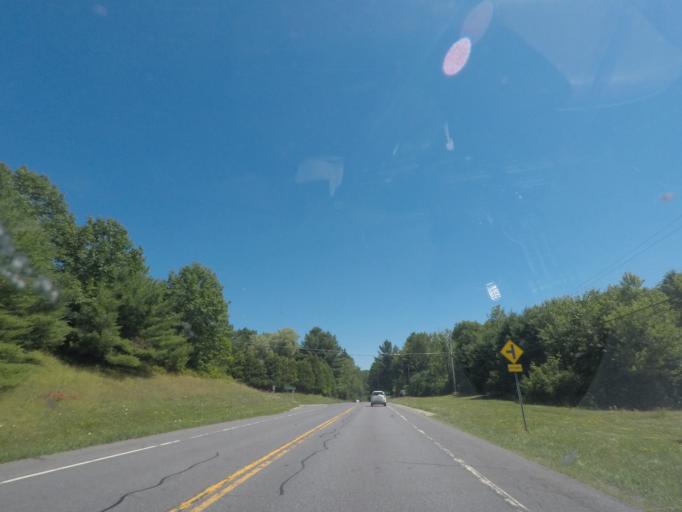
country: US
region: New York
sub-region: Rensselaer County
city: Averill Park
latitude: 42.6546
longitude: -73.5695
